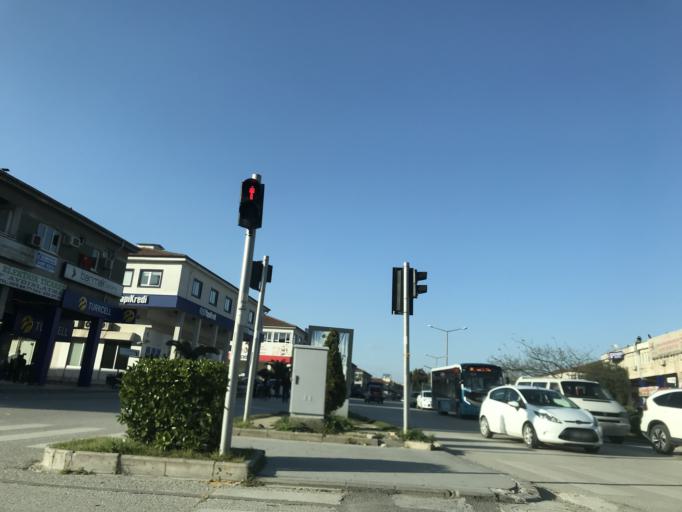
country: TR
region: Hatay
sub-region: Antakya Ilcesi
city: Antakya
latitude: 36.2090
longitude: 36.1651
